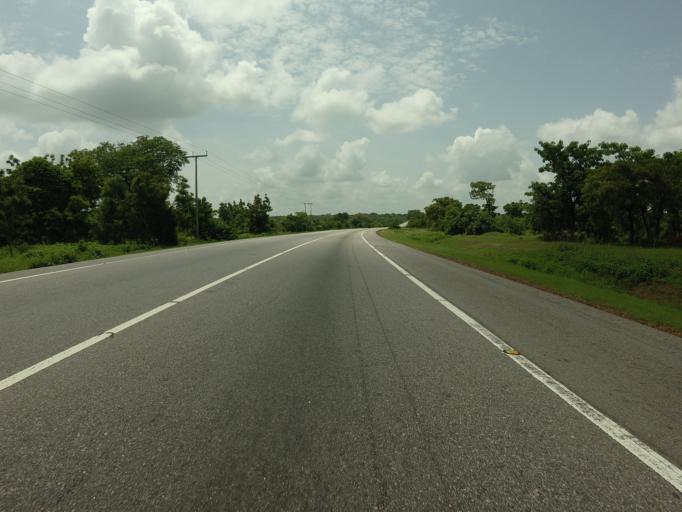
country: GH
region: Northern
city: Tamale
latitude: 9.1315
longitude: -1.2438
